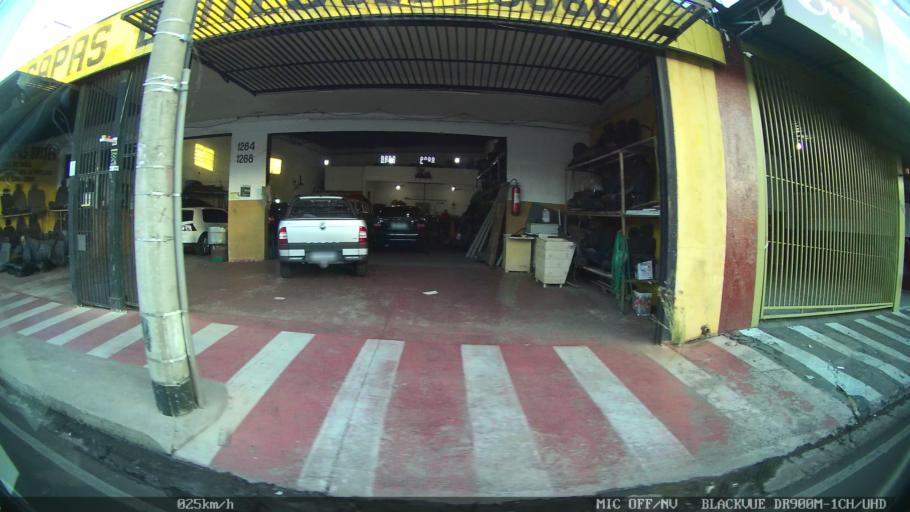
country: BR
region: Sao Paulo
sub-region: Sao Jose Do Rio Preto
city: Sao Jose do Rio Preto
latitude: -20.8039
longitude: -49.3624
